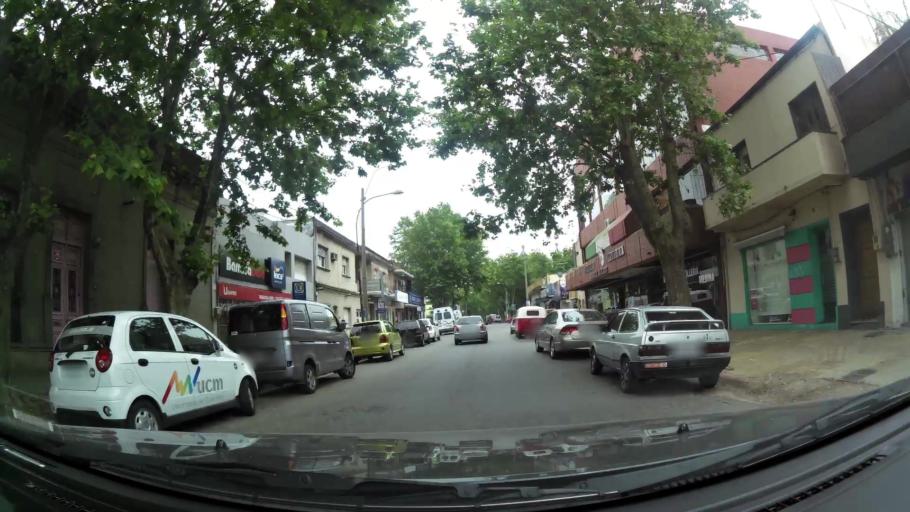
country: UY
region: Canelones
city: Las Piedras
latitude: -34.7279
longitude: -56.2150
